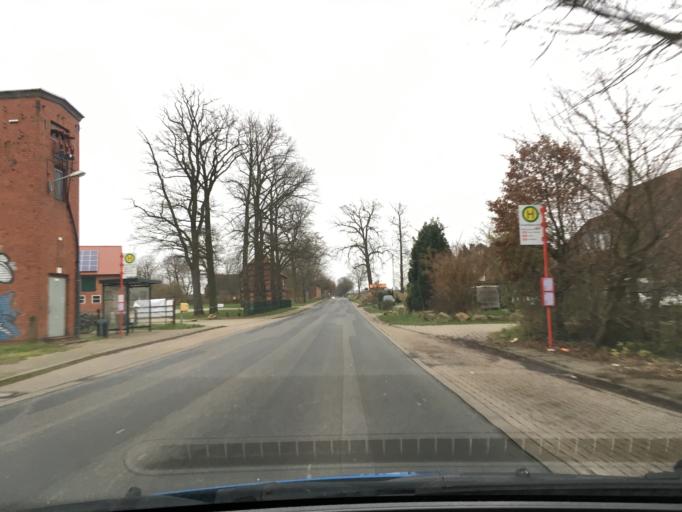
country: DE
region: Lower Saxony
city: Reinstorf
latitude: 53.2652
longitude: 10.5621
